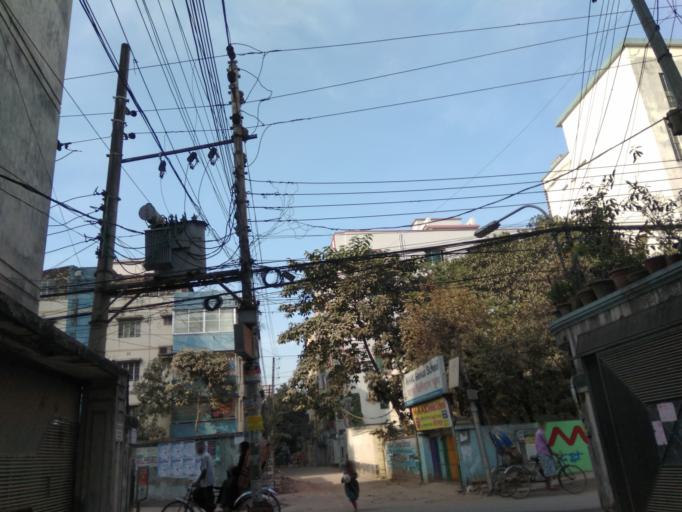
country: BD
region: Dhaka
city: Azimpur
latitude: 23.7711
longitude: 90.3570
